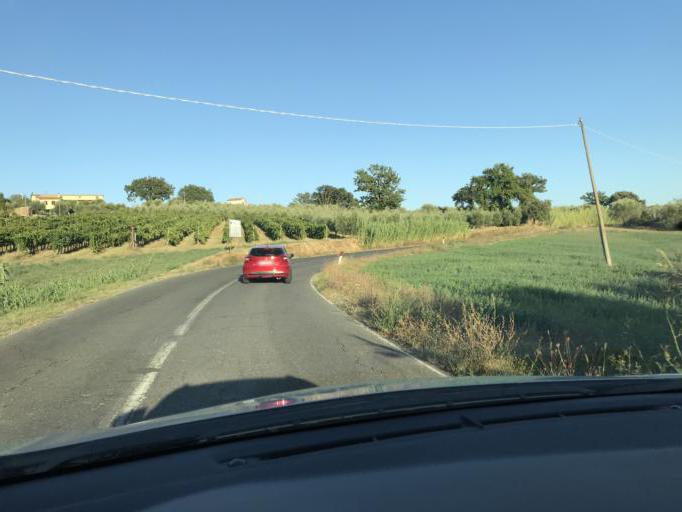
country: IT
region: Umbria
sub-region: Provincia di Terni
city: Amelia
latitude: 42.5281
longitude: 12.4076
